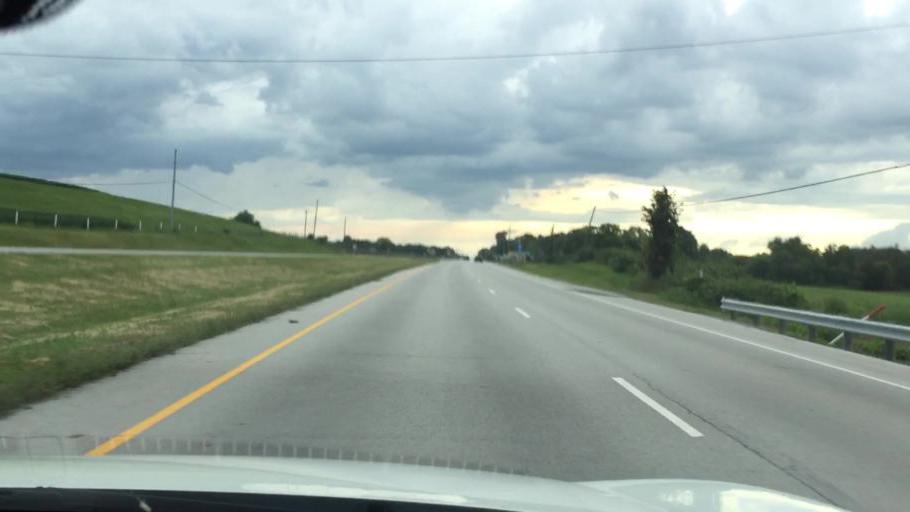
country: US
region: Ohio
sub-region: Clark County
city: Northridge
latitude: 39.9233
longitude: -83.7118
